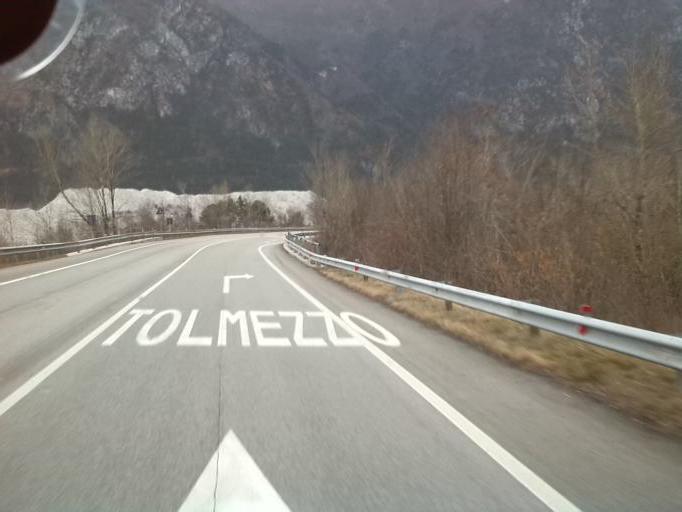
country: IT
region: Friuli Venezia Giulia
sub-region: Provincia di Udine
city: Amaro
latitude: 46.3796
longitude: 13.1332
